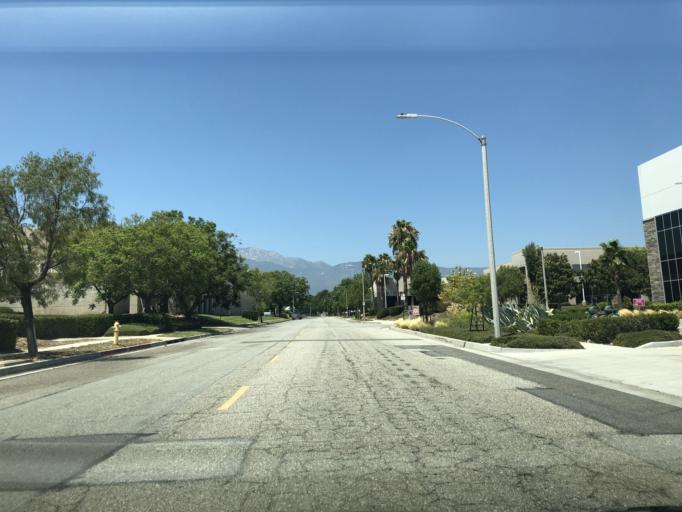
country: US
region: California
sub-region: San Bernardino County
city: Rancho Cucamonga
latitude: 34.0803
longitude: -117.5524
